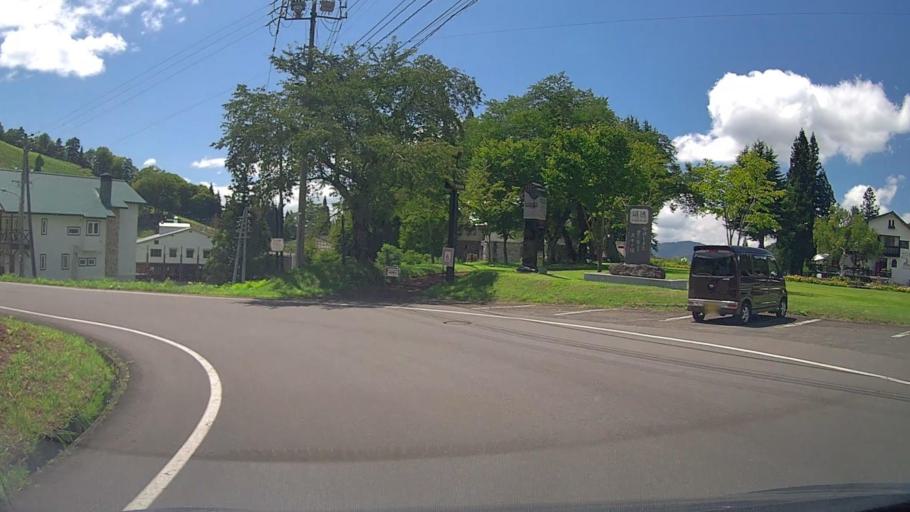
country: JP
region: Nagano
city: Iiyama
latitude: 36.9268
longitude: 138.4551
